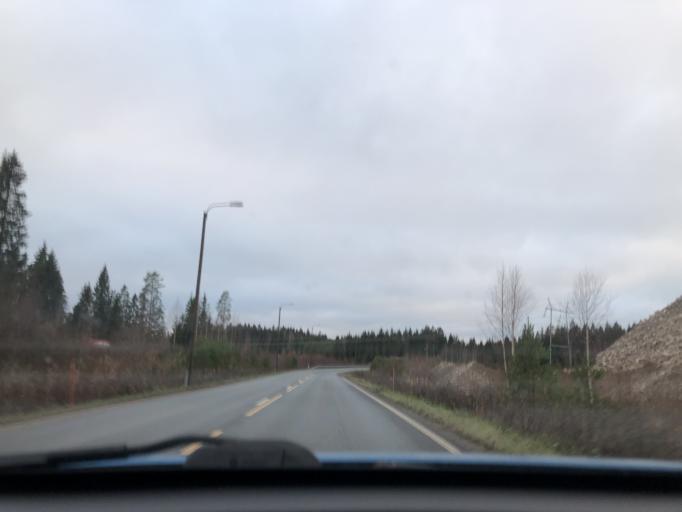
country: FI
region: Pirkanmaa
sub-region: Tampere
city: Kangasala
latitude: 61.5346
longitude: 23.9872
